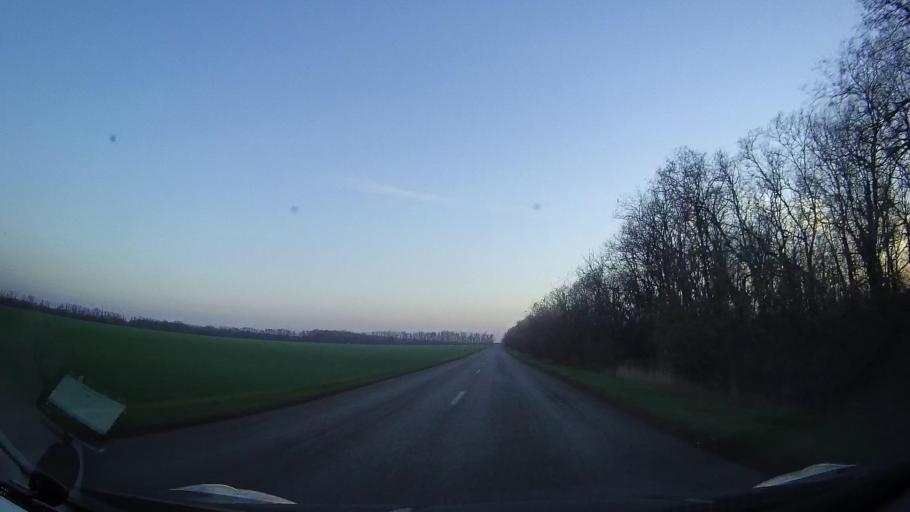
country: RU
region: Rostov
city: Zernograd
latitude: 46.9714
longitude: 40.3915
